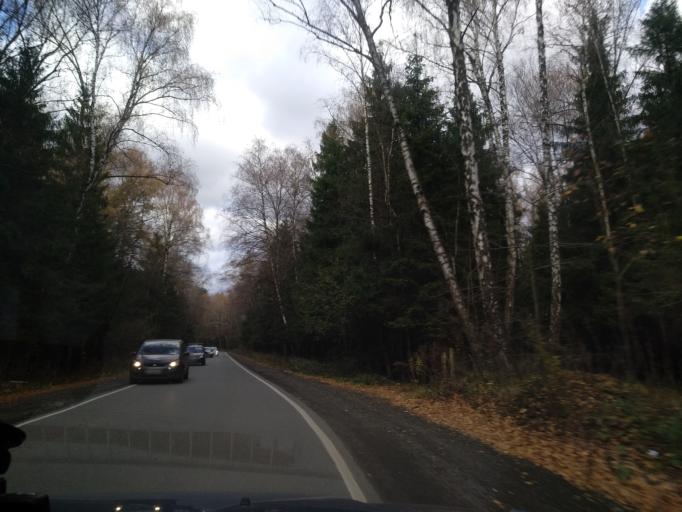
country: RU
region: Moscow
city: Lianozovo
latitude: 55.9122
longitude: 37.6104
